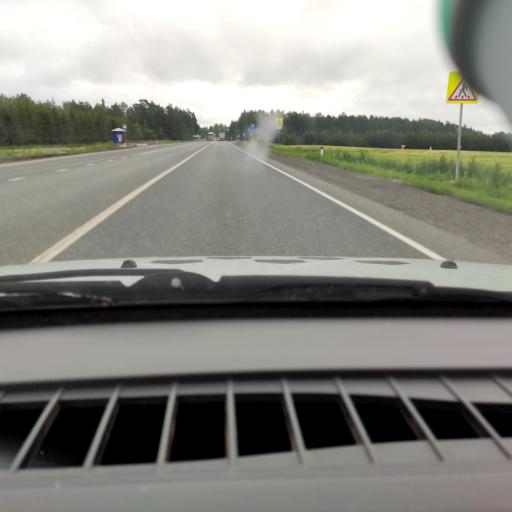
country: RU
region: Udmurtiya
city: Alnashi
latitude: 56.0841
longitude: 52.4172
